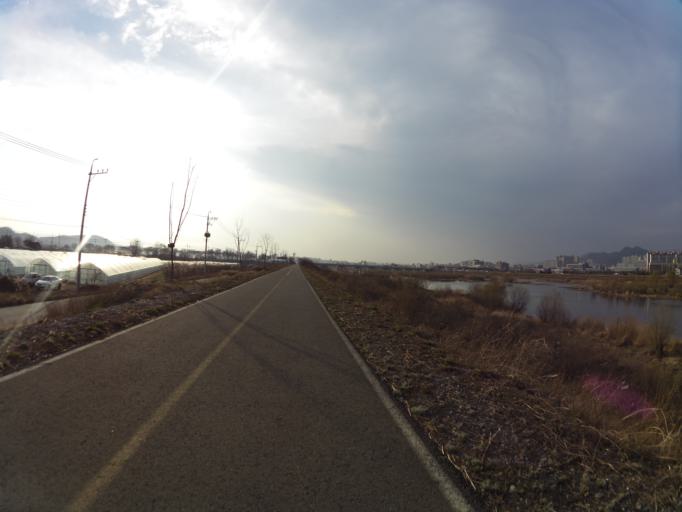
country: KR
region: Gyeongsangbuk-do
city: Gyeongsan-si
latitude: 35.8597
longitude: 128.7214
